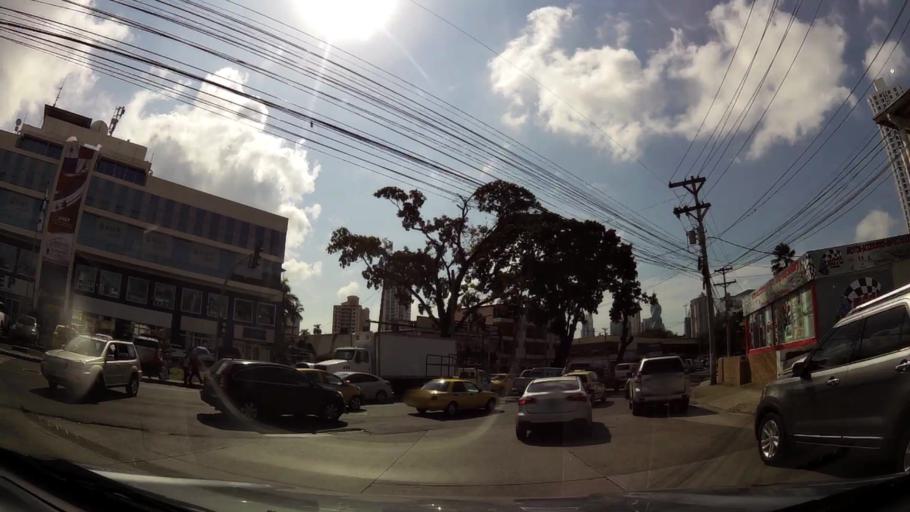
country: PA
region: Panama
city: Panama
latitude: 8.9955
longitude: -79.5193
